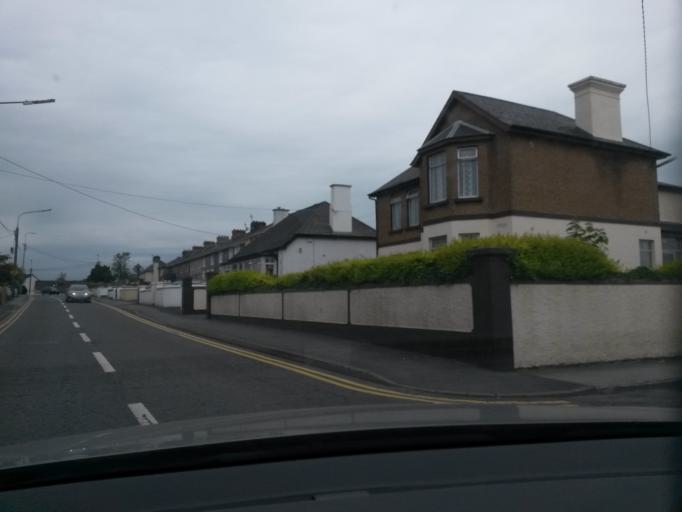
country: IE
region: Munster
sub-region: An Clar
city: Ennis
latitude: 52.8395
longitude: -8.9783
